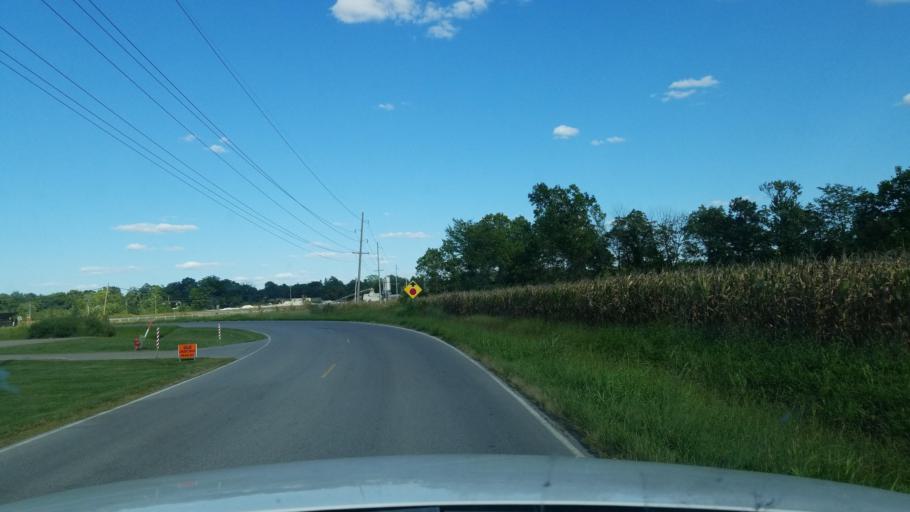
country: US
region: Illinois
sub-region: Saline County
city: Harrisburg
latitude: 37.7202
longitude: -88.5376
